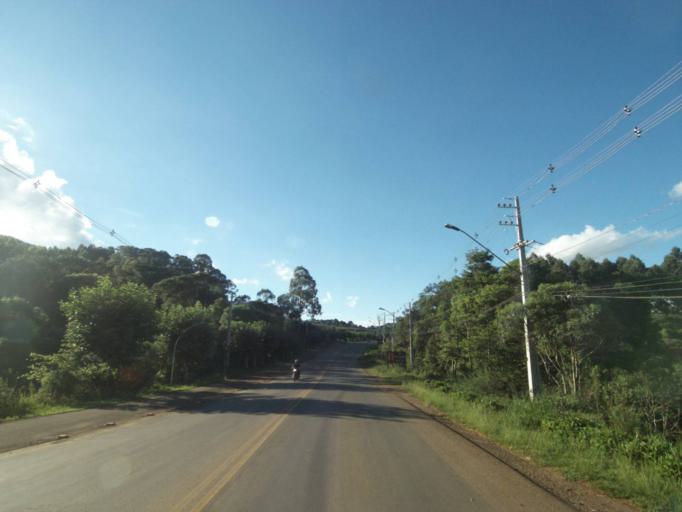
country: BR
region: Parana
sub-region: Uniao Da Vitoria
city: Uniao da Vitoria
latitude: -26.1592
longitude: -51.5401
